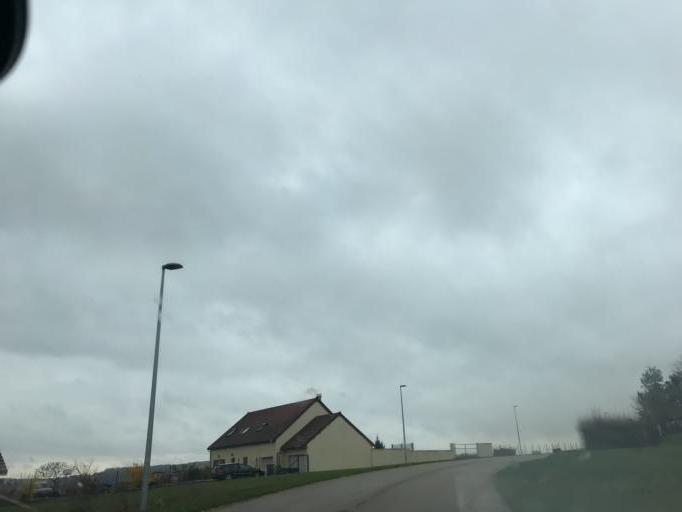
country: FR
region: Bourgogne
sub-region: Departement de l'Yonne
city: Fontenailles
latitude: 47.6110
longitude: 3.4972
